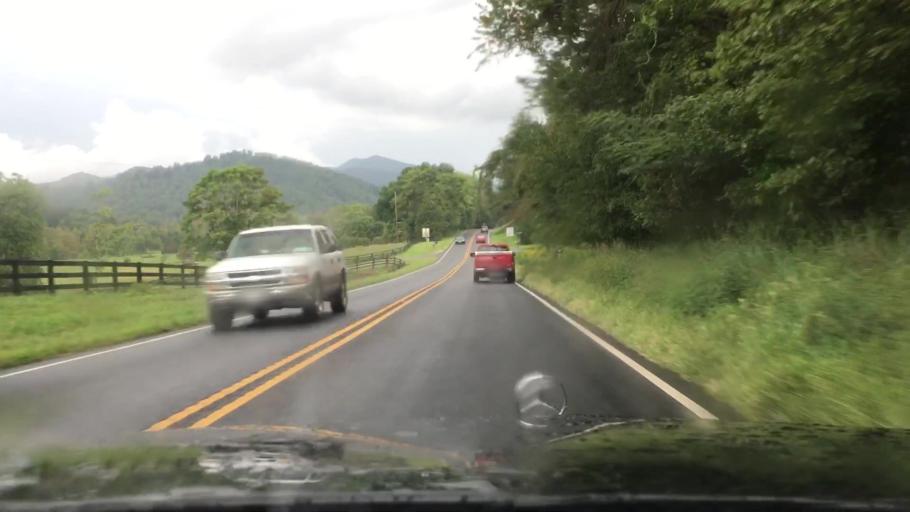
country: US
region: Virginia
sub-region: Nelson County
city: Nellysford
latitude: 37.8962
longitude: -78.8636
